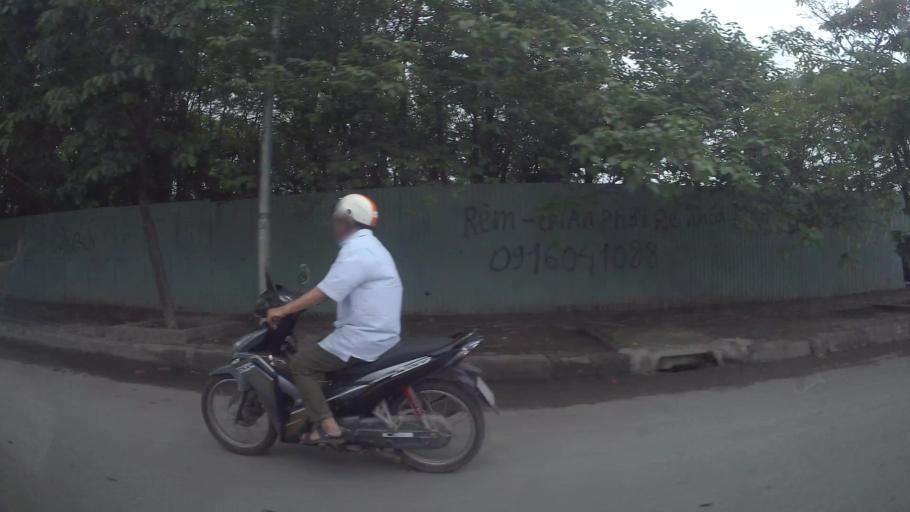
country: VN
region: Ha Noi
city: Van Dien
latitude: 20.9655
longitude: 105.8539
